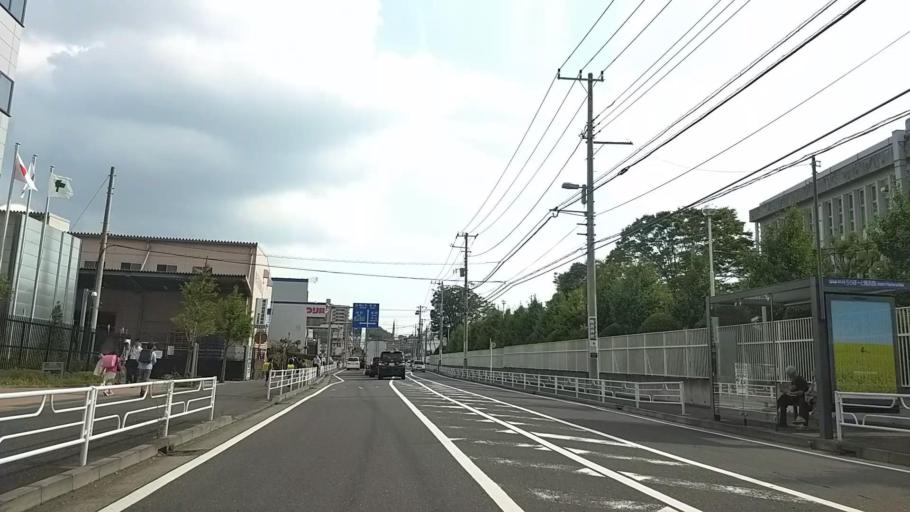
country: JP
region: Kanagawa
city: Yokohama
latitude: 35.5165
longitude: 139.5635
